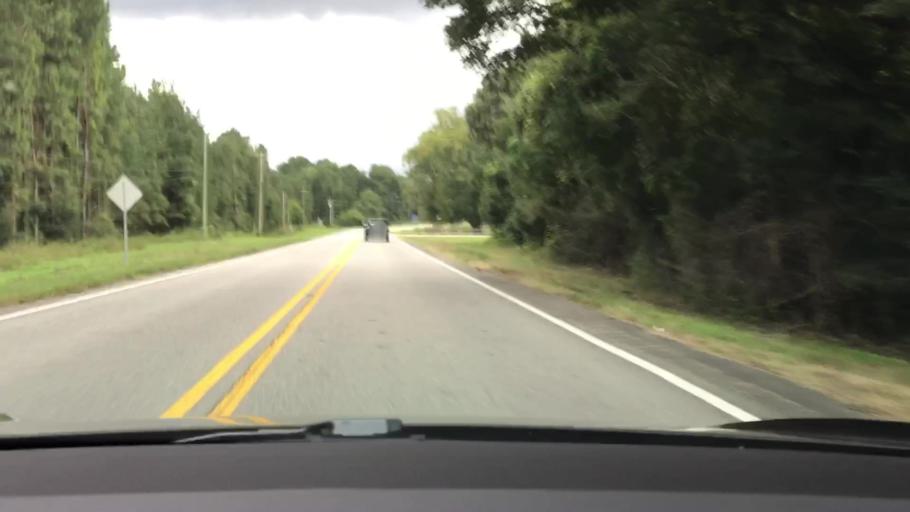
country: US
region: Alabama
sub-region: Coffee County
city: Elba
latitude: 31.4884
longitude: -86.0533
